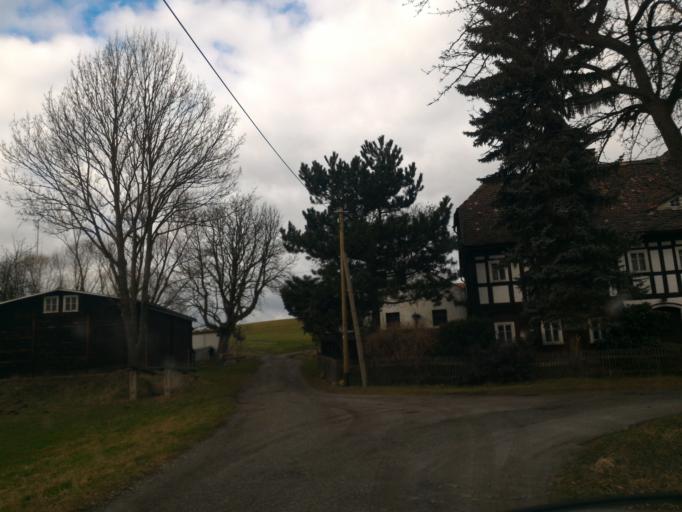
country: DE
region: Saxony
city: Grossschonau
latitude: 50.8877
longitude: 14.6500
